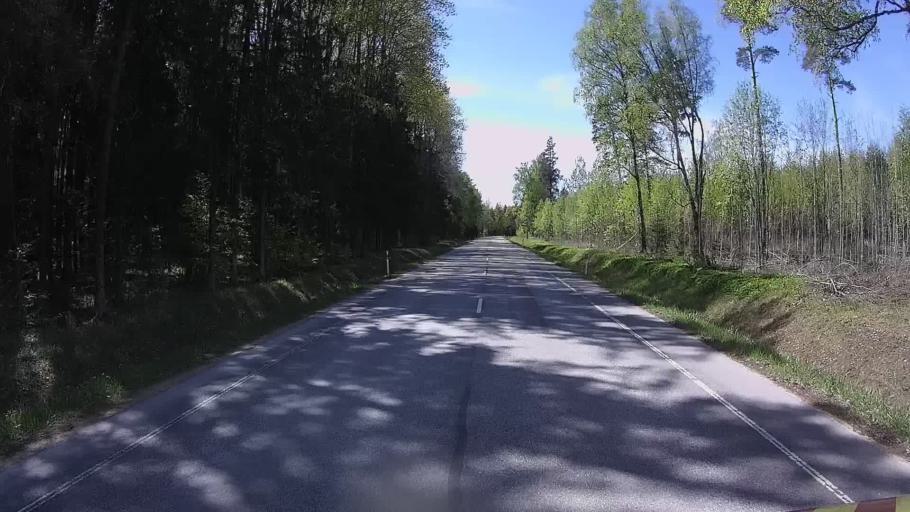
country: EE
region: Vorumaa
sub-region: Voru linn
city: Voru
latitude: 57.8844
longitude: 27.1468
